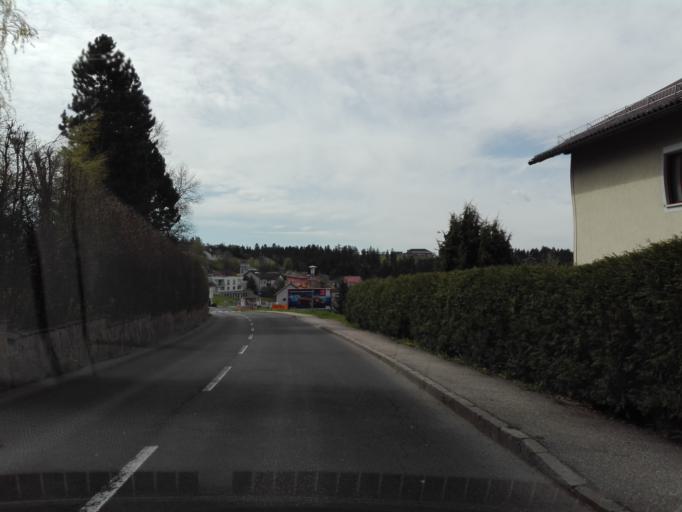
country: AT
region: Upper Austria
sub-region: Politischer Bezirk Urfahr-Umgebung
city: Gramastetten
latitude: 48.3795
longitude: 14.1932
